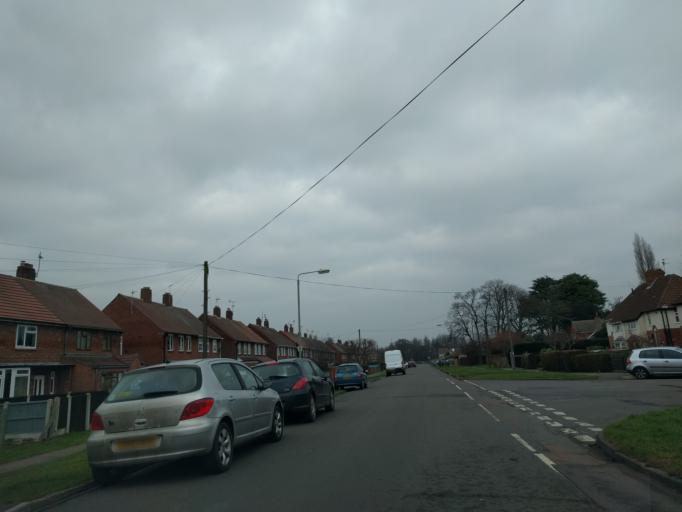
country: GB
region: England
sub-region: Nottinghamshire
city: Newark on Trent
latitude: 53.0917
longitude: -0.7953
